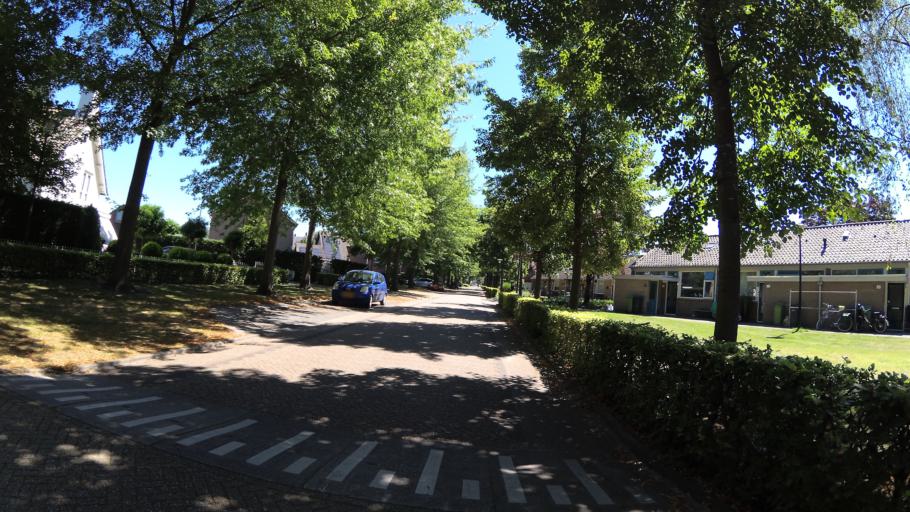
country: NL
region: North Brabant
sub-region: Gemeente Waalwijk
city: Waalwijk
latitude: 51.6721
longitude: 5.0458
